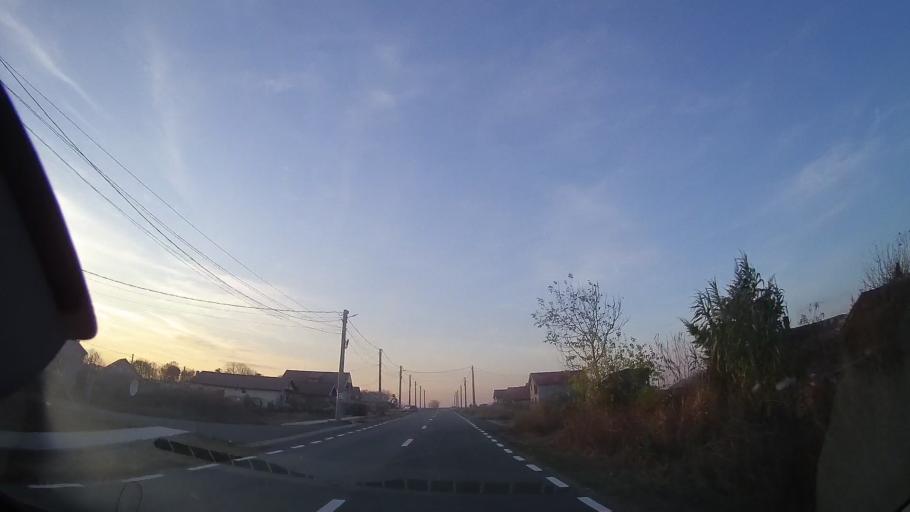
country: RO
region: Constanta
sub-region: Comuna Topraisar
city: Topraisar
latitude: 44.0118
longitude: 28.4420
